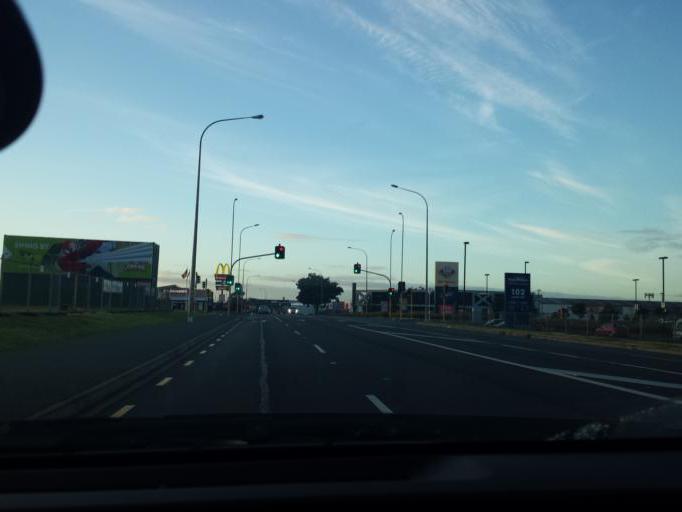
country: NZ
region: Auckland
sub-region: Auckland
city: Tamaki
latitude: -36.8888
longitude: 174.8323
